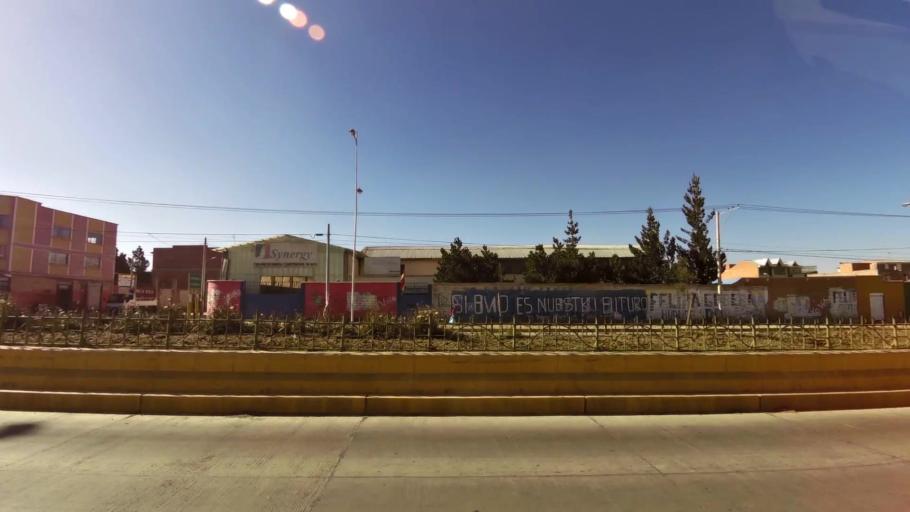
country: BO
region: La Paz
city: La Paz
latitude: -16.5273
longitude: -68.1841
